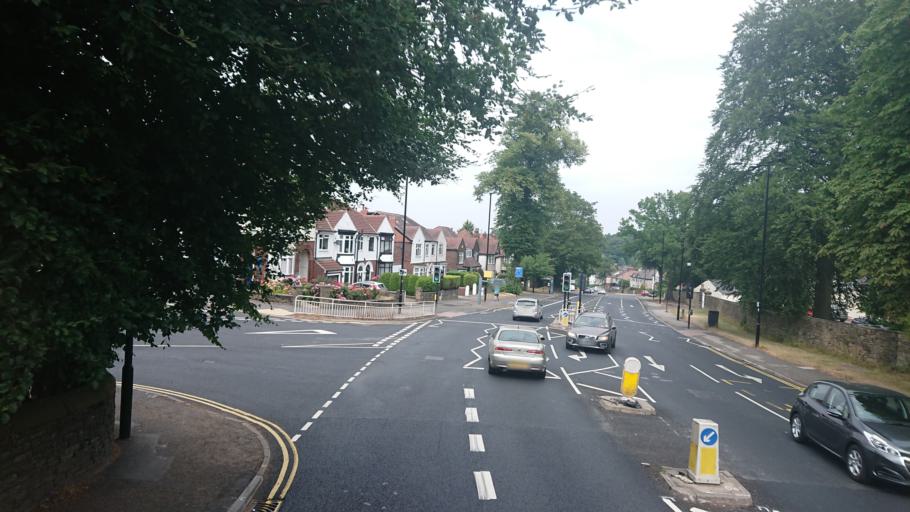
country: GB
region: England
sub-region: Sheffield
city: Sheffield
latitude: 53.3574
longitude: -1.5104
